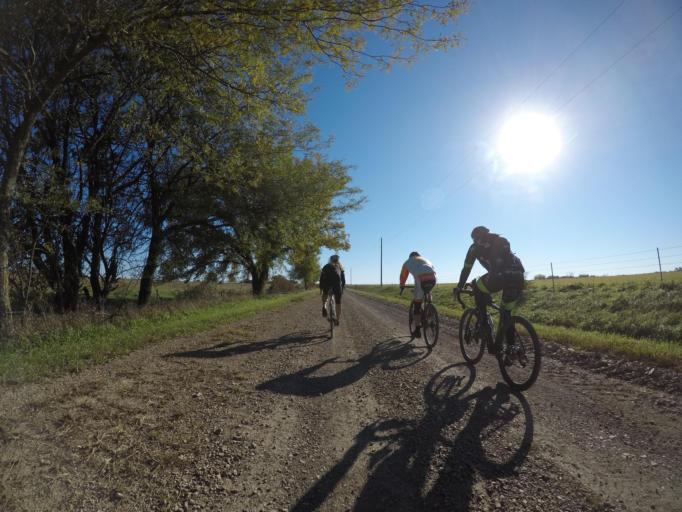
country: US
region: Kansas
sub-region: Morris County
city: Council Grove
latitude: 38.8259
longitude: -96.4533
